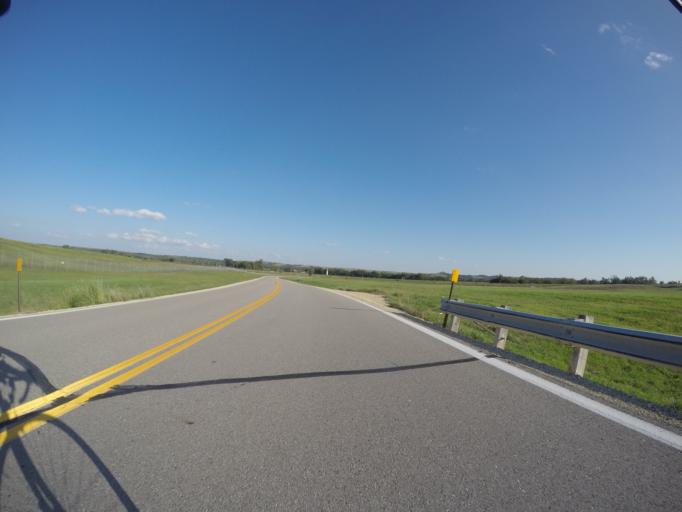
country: US
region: Kansas
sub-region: Riley County
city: Ogden
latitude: 39.1276
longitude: -96.6875
